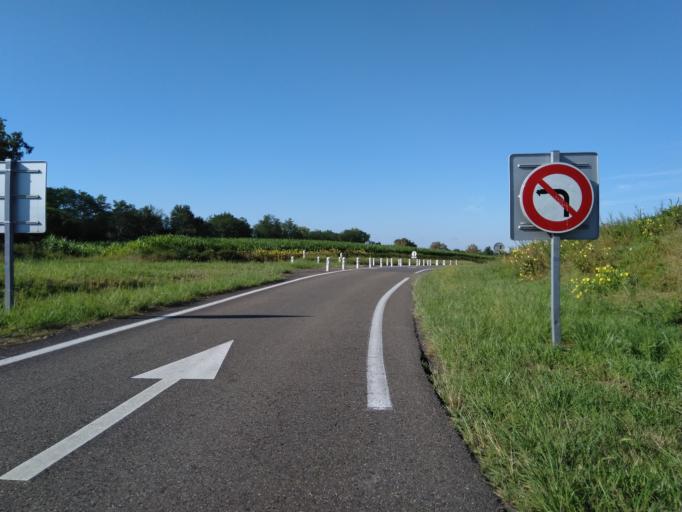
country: FR
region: Aquitaine
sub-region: Departement des Landes
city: Saint-Vincent-de-Paul
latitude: 43.7365
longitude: -1.0268
